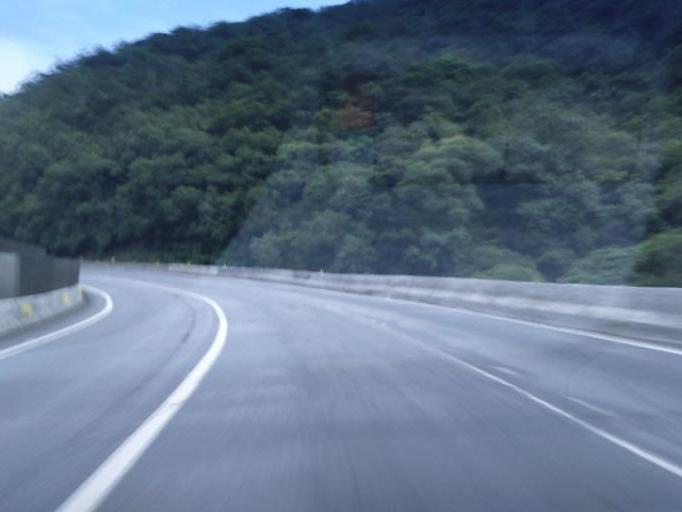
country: BR
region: Parana
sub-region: Guaratuba
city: Guaratuba
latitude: -25.8715
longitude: -48.9372
